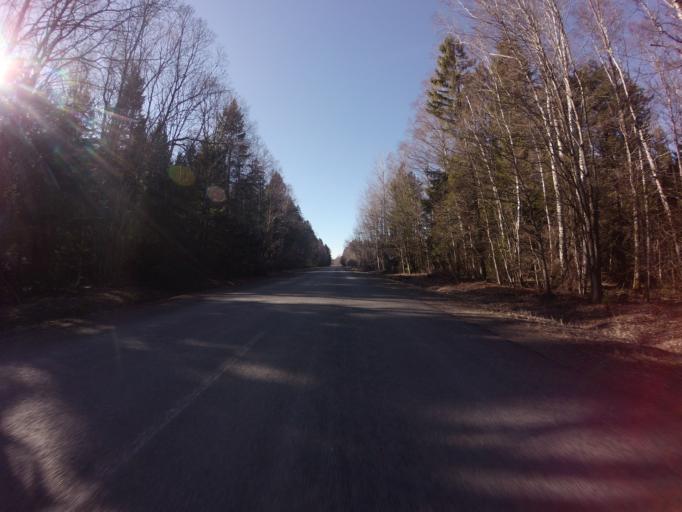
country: EE
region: Saare
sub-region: Kuressaare linn
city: Kuressaare
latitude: 58.5734
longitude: 22.6641
